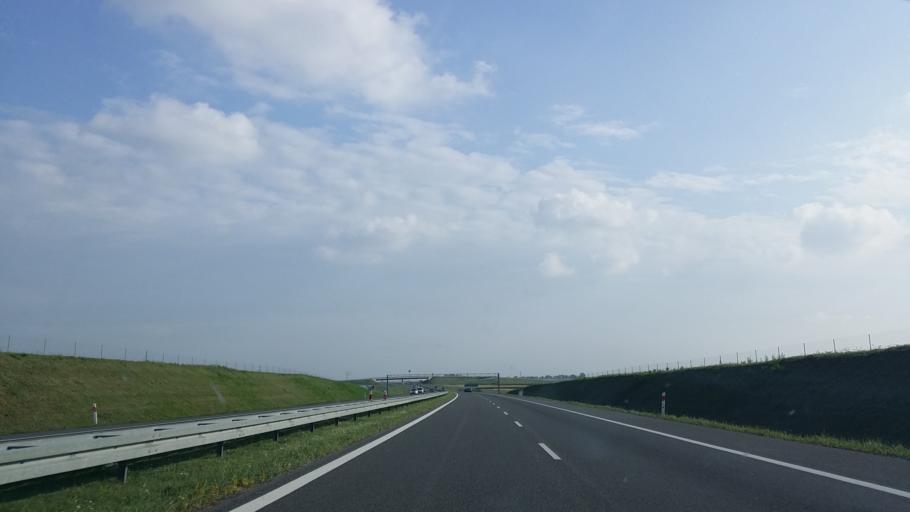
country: PL
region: Lubusz
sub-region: Powiat swiebodzinski
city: Swiebodzin
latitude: 52.3093
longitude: 15.5447
